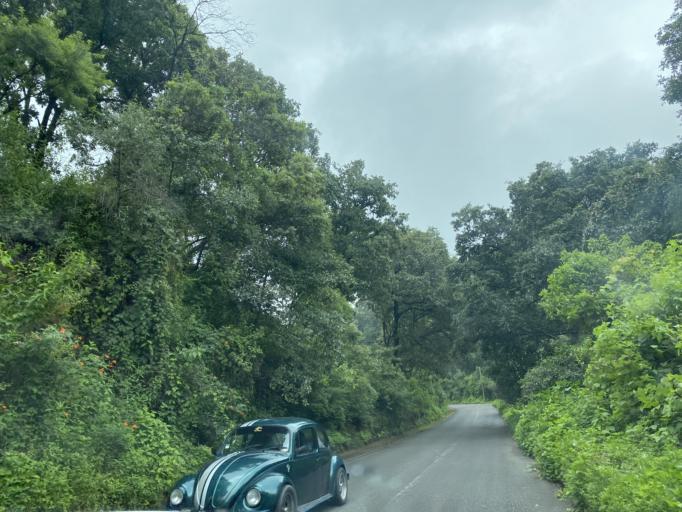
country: MX
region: Morelos
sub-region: Yecapixtla
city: Achichipico
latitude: 18.9388
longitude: -98.8160
